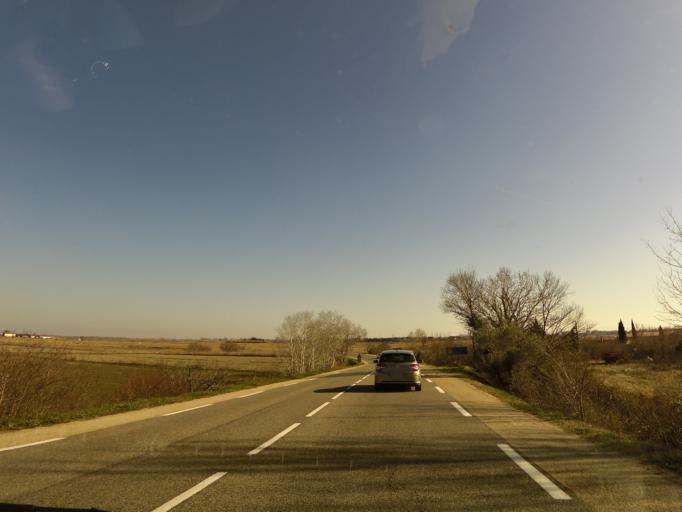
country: FR
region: Provence-Alpes-Cote d'Azur
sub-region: Departement des Bouches-du-Rhone
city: Saintes-Maries-de-la-Mer
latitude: 43.5456
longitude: 4.3513
